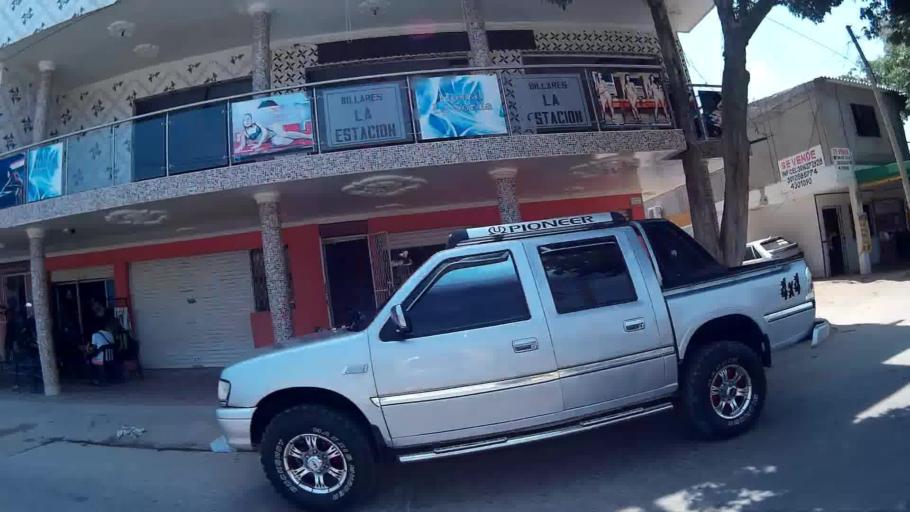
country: CO
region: Magdalena
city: Santa Marta
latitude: 11.2204
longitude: -74.1914
